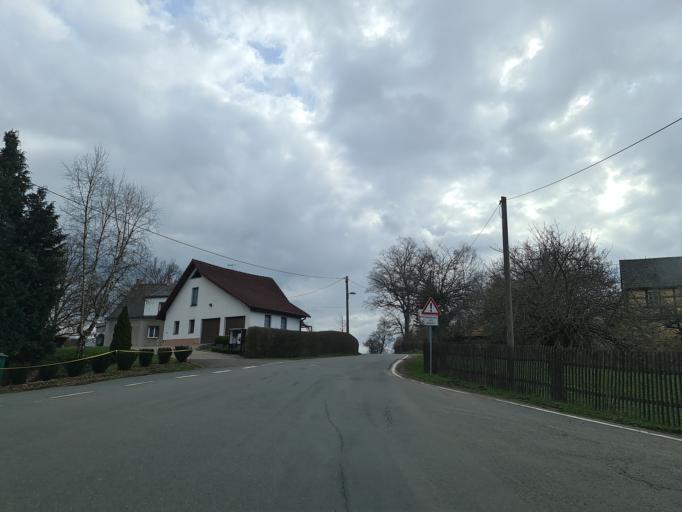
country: DE
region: Saxony
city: Wildenfels
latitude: 50.6990
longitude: 12.6176
